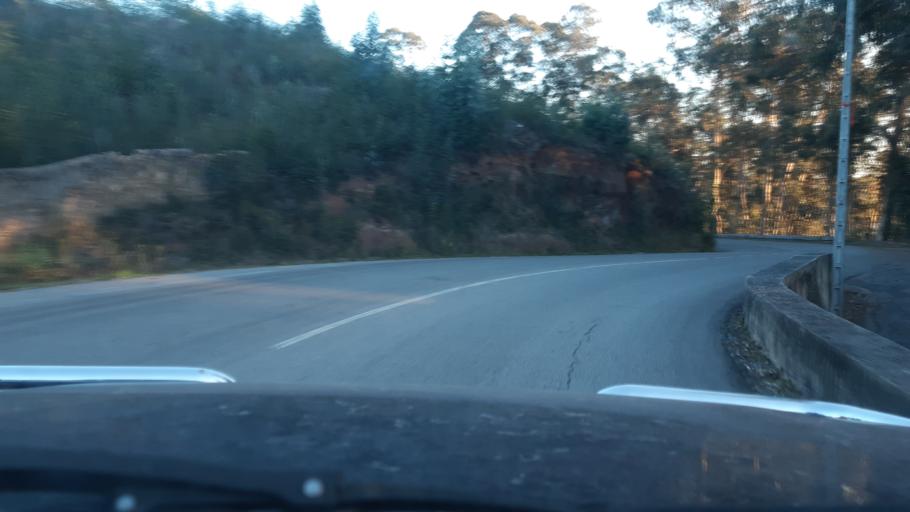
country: PT
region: Aveiro
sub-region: Agueda
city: Agueda
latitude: 40.5781
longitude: -8.4628
